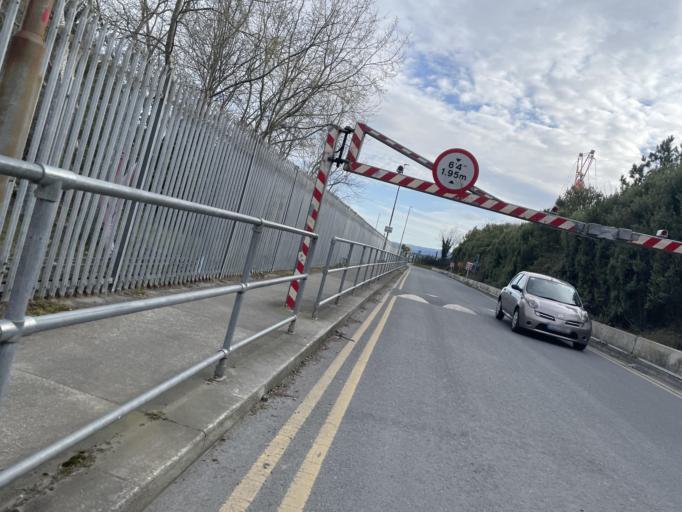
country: IE
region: Leinster
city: Sandymount
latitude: 53.3387
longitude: -6.1929
